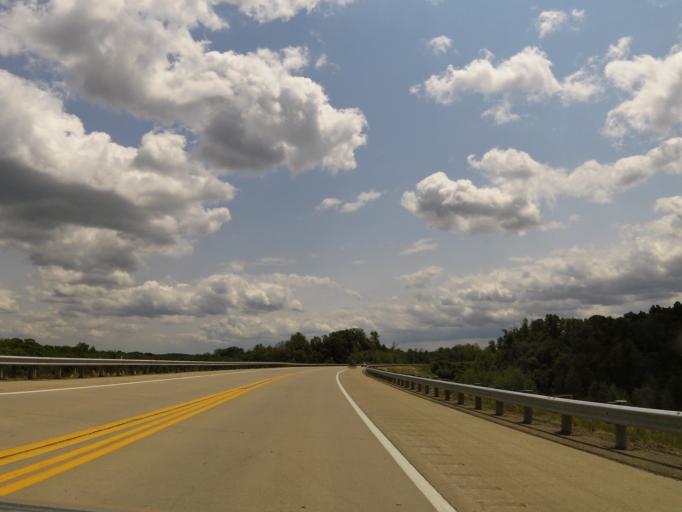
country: US
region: Ohio
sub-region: Athens County
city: Athens
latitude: 39.2716
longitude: -82.0891
